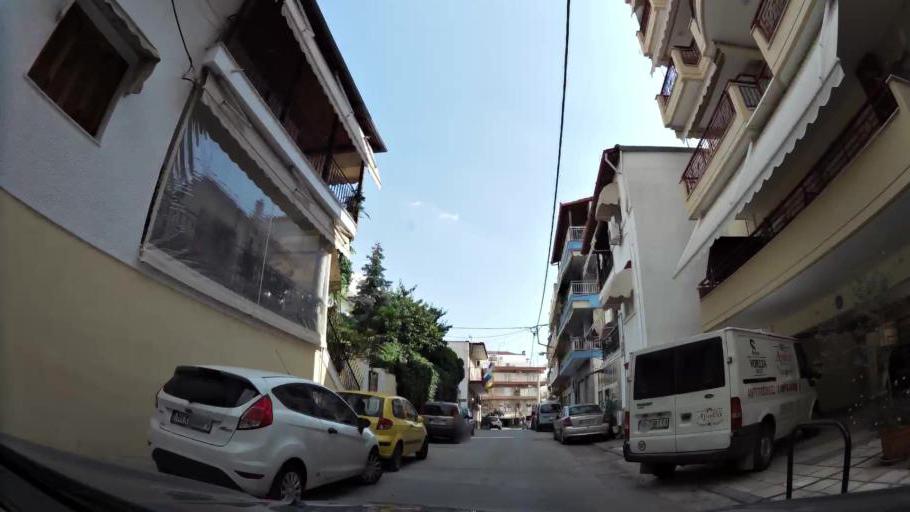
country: GR
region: Central Macedonia
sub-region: Nomos Thessalonikis
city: Polichni
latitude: 40.6624
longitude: 22.9494
